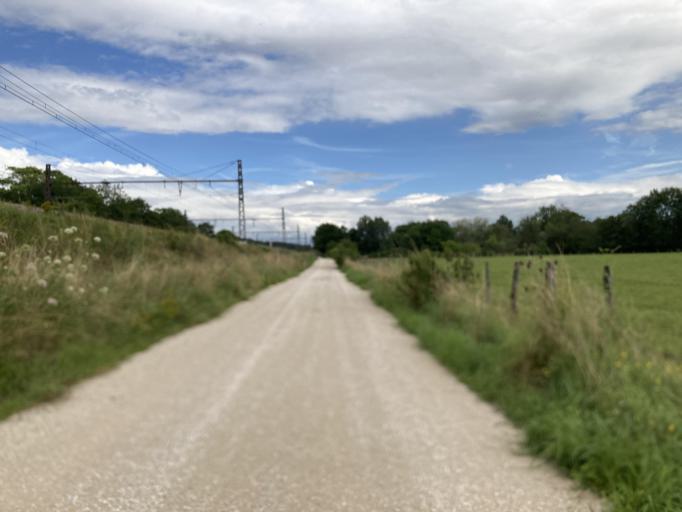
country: FR
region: Bourgogne
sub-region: Departement de la Cote-d'Or
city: Montbard
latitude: 47.6170
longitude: 4.3741
